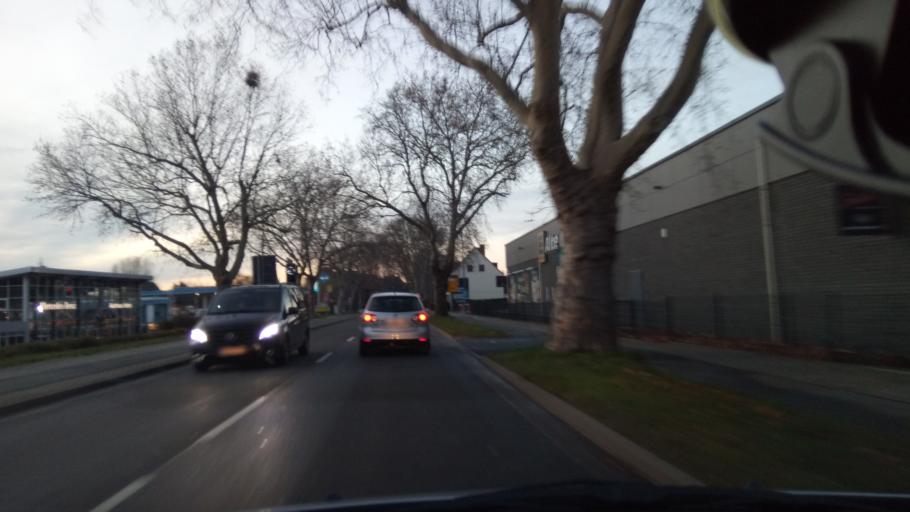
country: DE
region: Saxony
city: Bitterfeld-Wolfen
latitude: 51.6267
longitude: 12.3383
